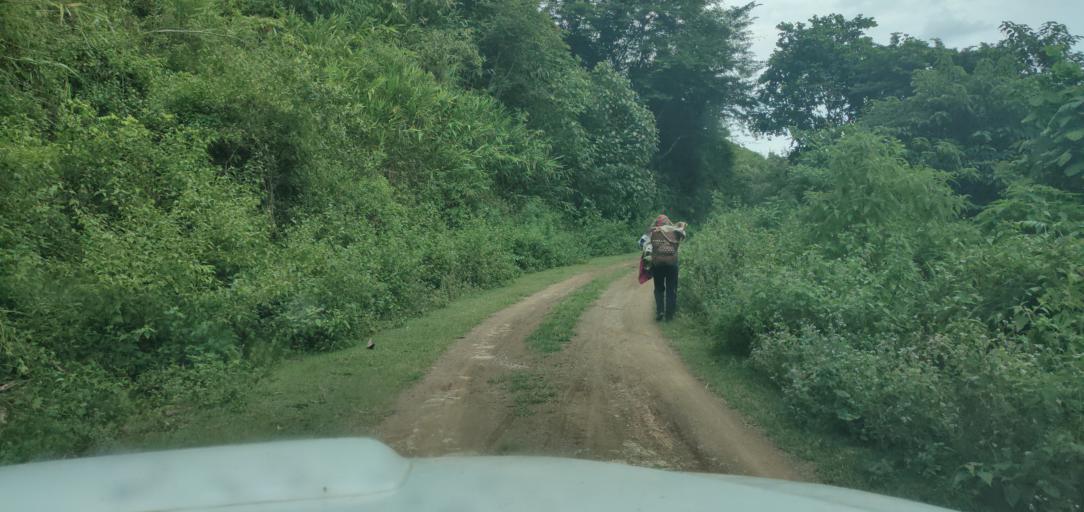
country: LA
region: Phongsali
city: Phongsali
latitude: 21.4472
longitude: 102.3145
